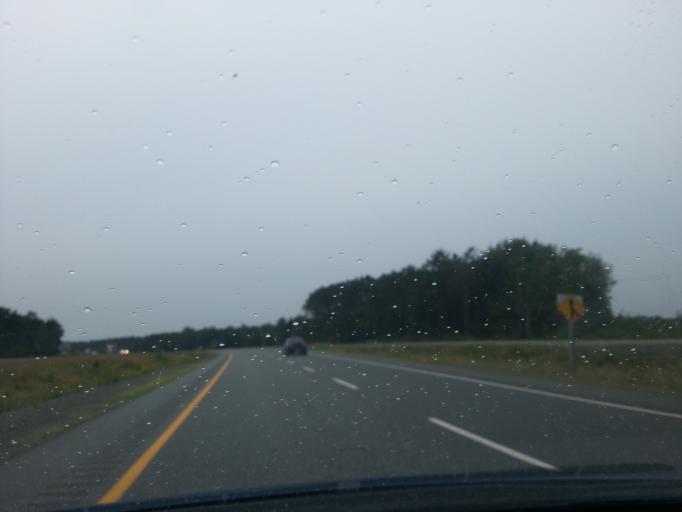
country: CA
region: Nova Scotia
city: Truro
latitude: 45.3984
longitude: -63.4324
